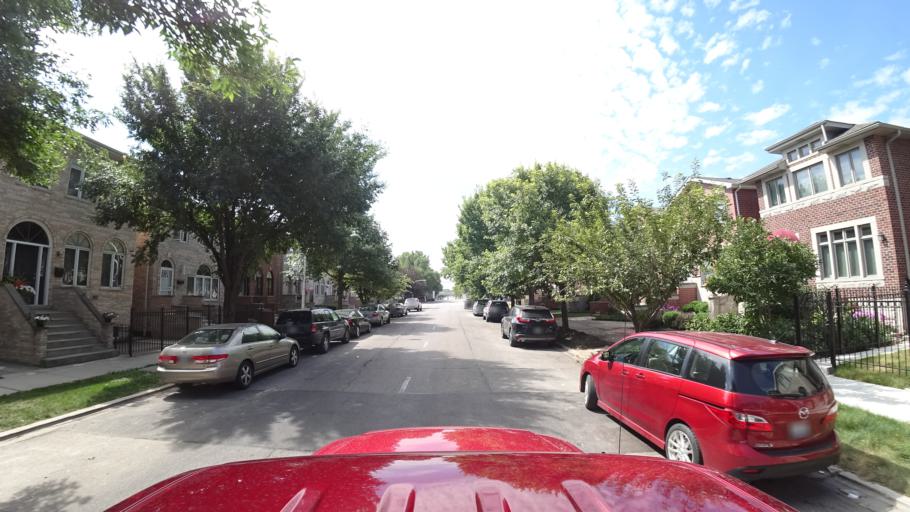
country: US
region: Illinois
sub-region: Cook County
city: Chicago
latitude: 41.8244
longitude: -87.6448
